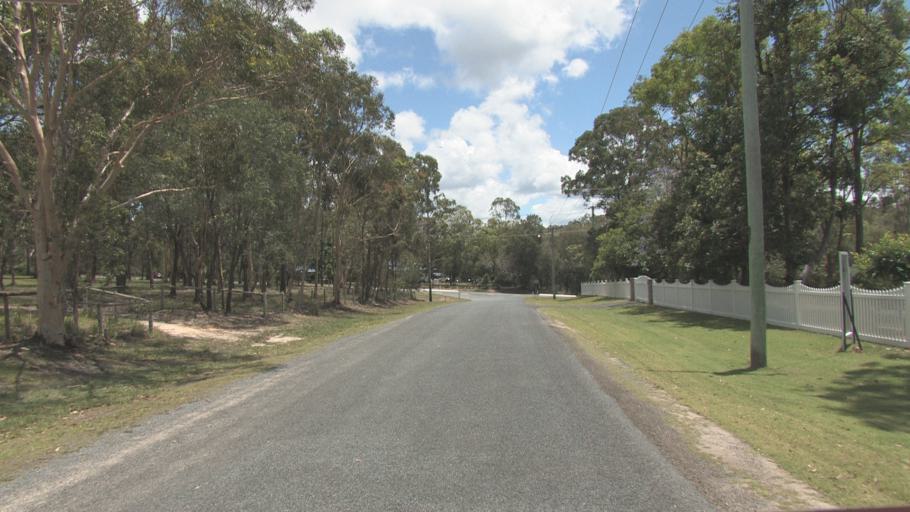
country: AU
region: Queensland
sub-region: Redland
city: Redland Bay
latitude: -27.6651
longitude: 153.2772
